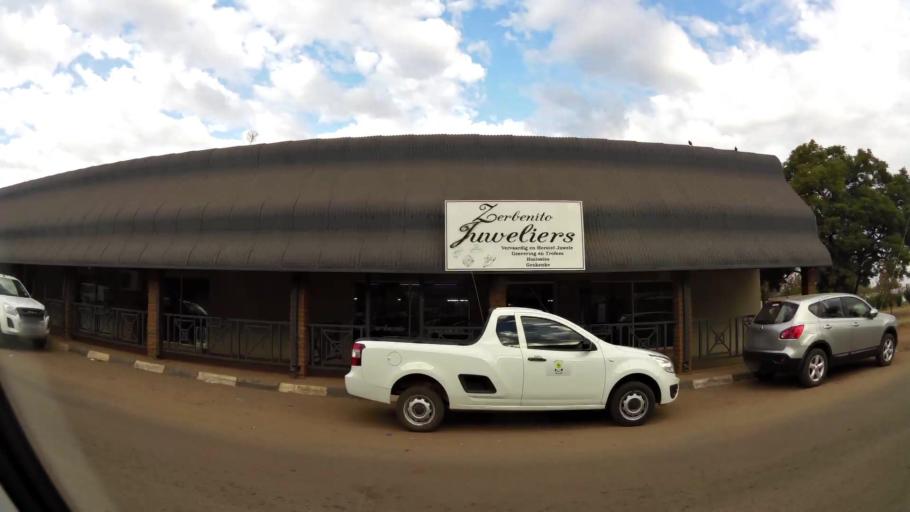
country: ZA
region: Limpopo
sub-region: Waterberg District Municipality
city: Modimolle
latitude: -24.5197
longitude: 28.7120
